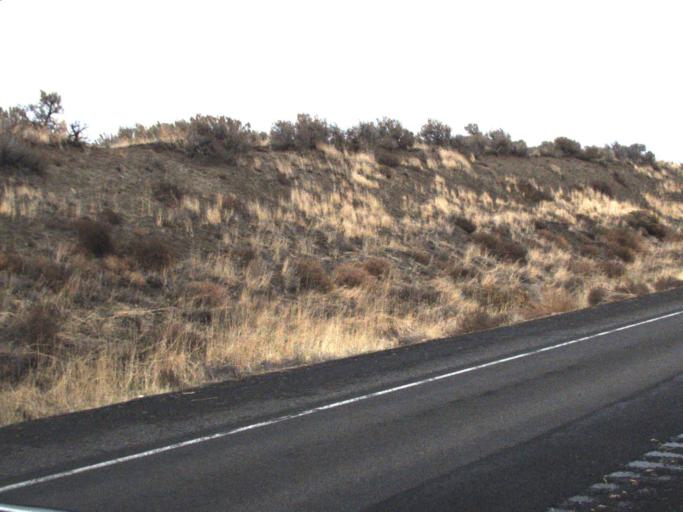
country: US
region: Washington
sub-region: Benton County
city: Finley
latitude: 46.0530
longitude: -118.8807
